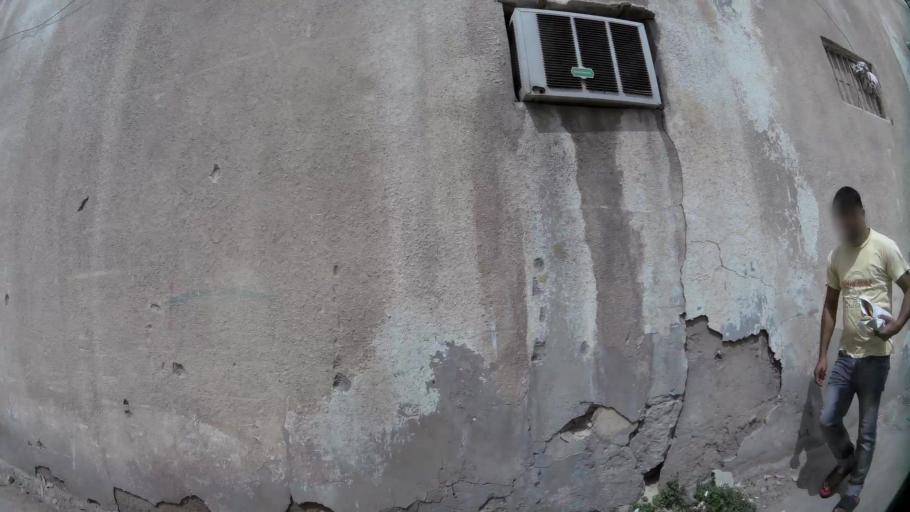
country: QA
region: Baladiyat ad Dawhah
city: Doha
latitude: 25.2754
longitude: 51.5241
